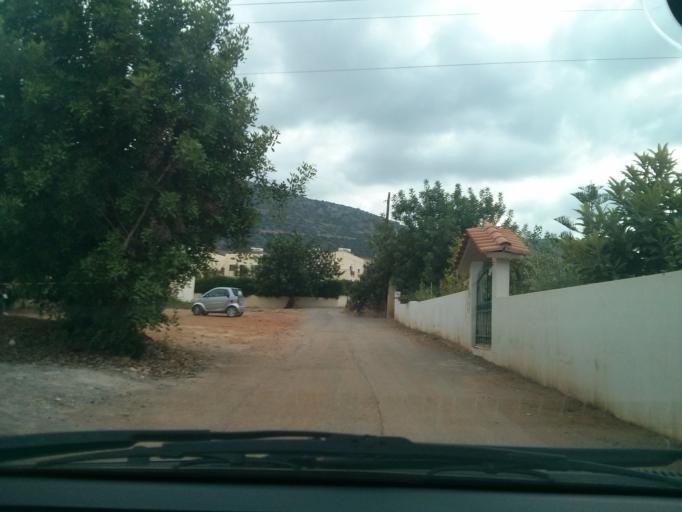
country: GR
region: Crete
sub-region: Nomos Irakleiou
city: Stalis
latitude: 35.2958
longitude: 25.4215
